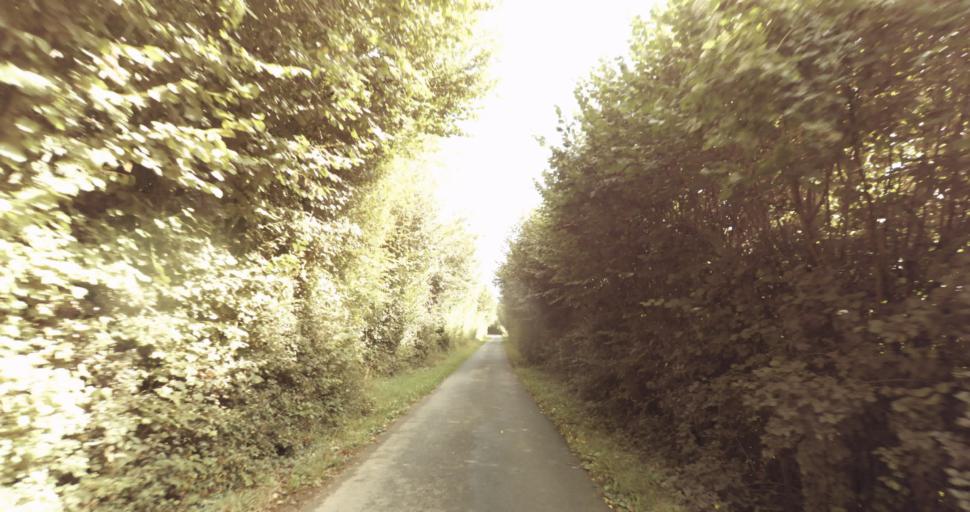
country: FR
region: Lower Normandy
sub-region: Departement de l'Orne
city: Gace
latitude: 48.8124
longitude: 0.2535
